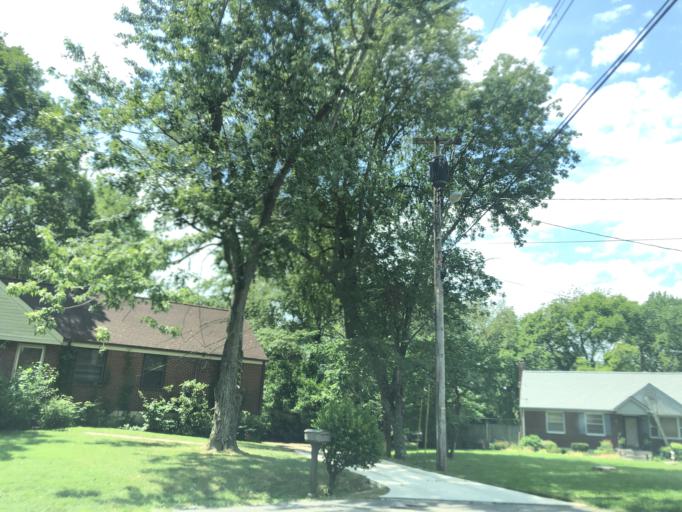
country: US
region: Tennessee
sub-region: Davidson County
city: Lakewood
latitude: 36.1549
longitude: -86.6498
